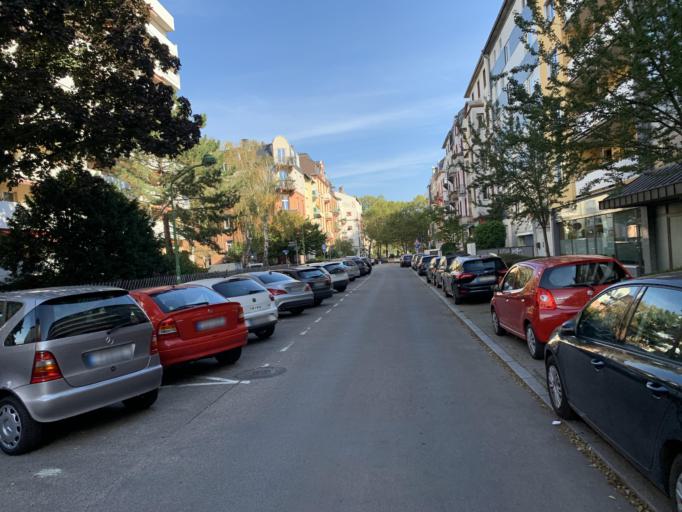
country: DE
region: Hesse
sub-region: Regierungsbezirk Darmstadt
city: Frankfurt am Main
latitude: 50.1227
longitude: 8.7081
